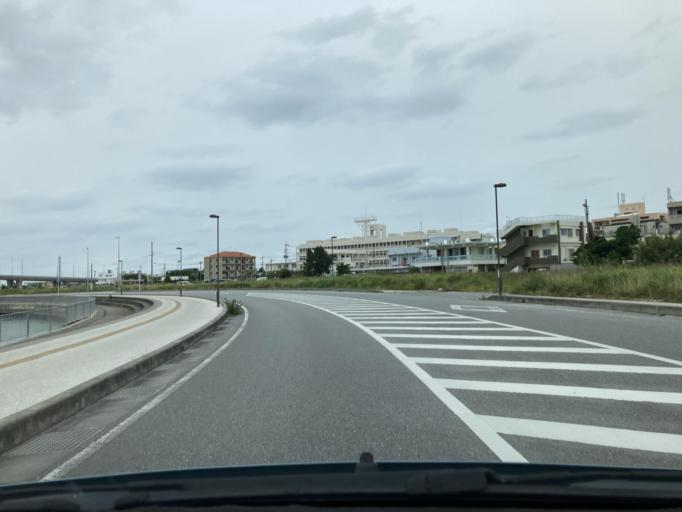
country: JP
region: Okinawa
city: Itoman
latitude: 26.1338
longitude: 127.6684
